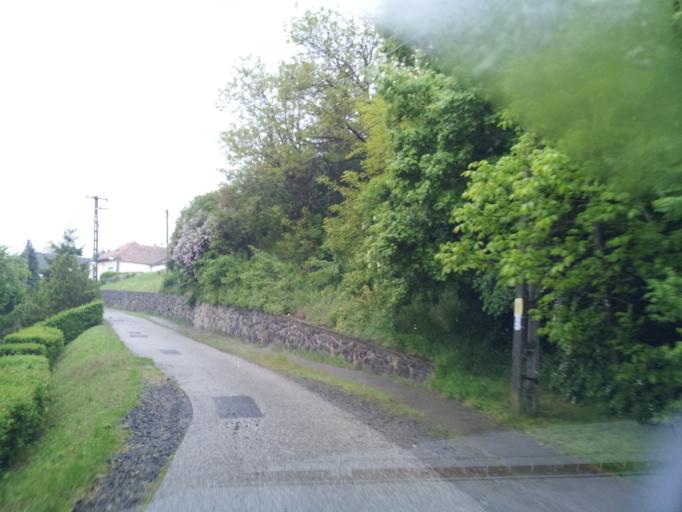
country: HU
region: Baranya
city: Hosszuheteny
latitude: 46.1694
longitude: 18.3479
